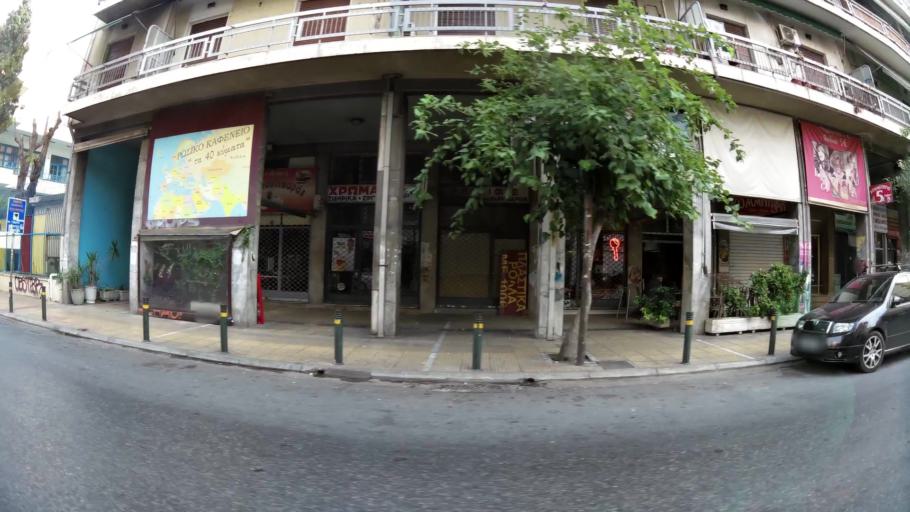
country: GR
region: Attica
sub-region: Nomarchia Athinas
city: Athens
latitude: 37.9899
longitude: 23.7243
